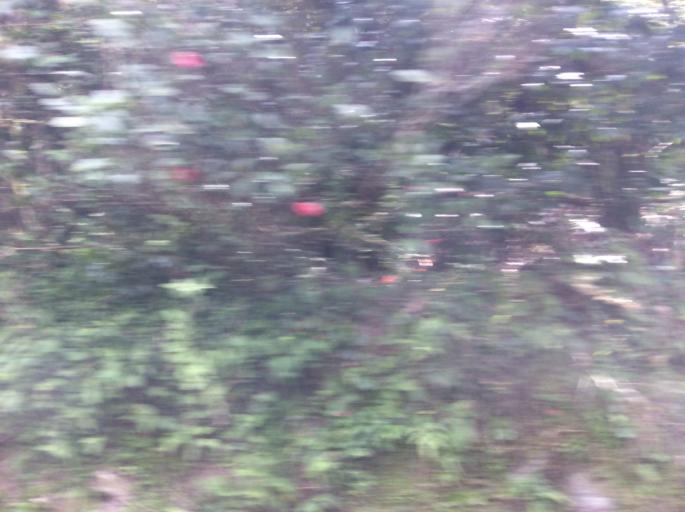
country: TW
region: Taipei
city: Taipei
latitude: 25.1648
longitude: 121.5439
